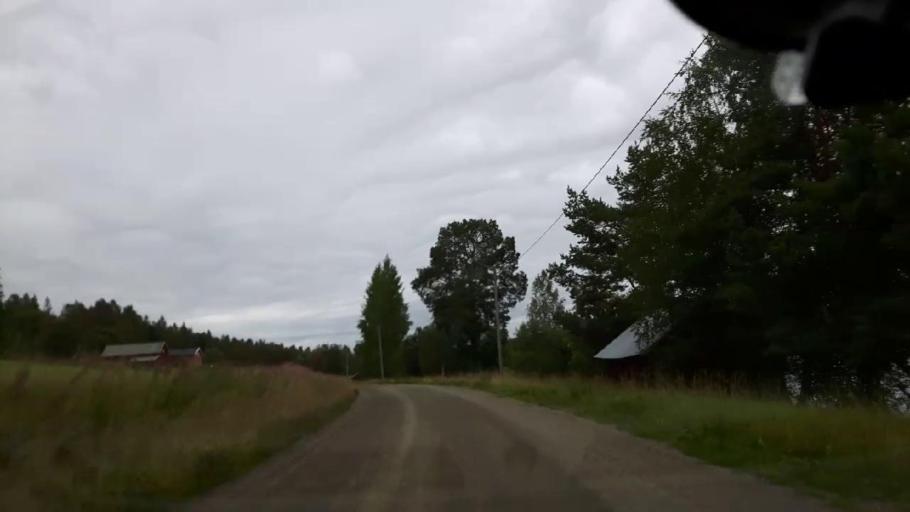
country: SE
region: Jaemtland
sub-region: Braecke Kommun
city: Braecke
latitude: 62.9935
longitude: 15.3834
